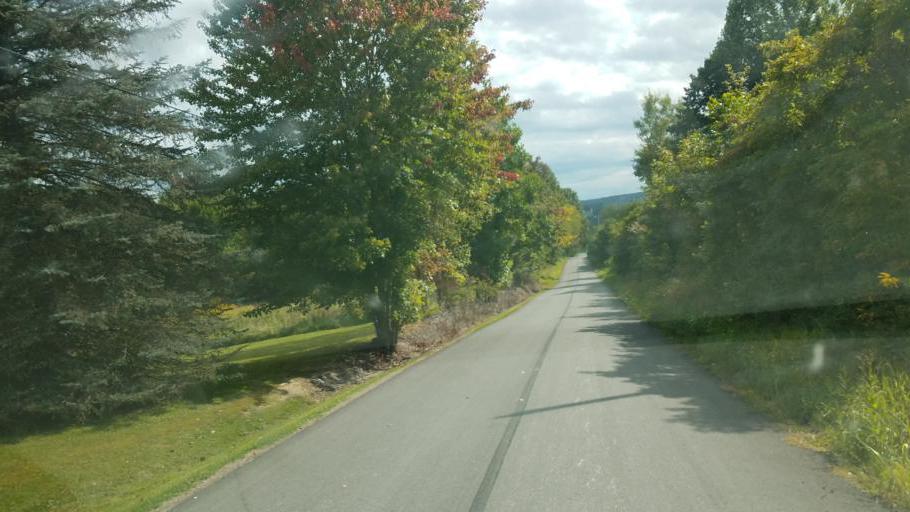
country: US
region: Pennsylvania
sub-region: Mercer County
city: Greenville
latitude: 41.5159
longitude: -80.3770
